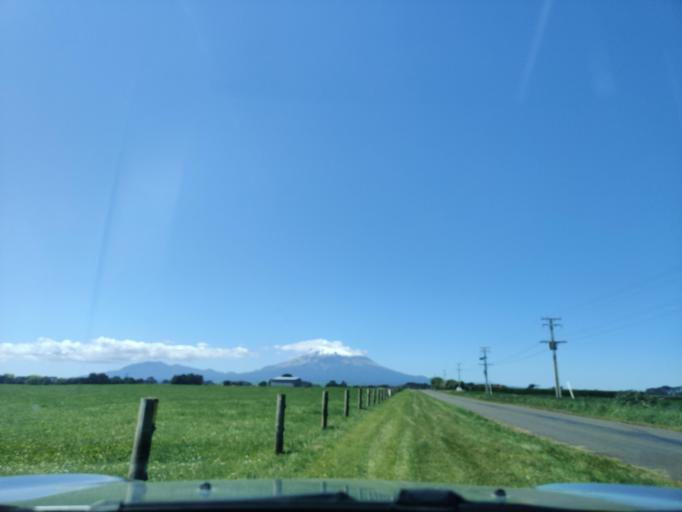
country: NZ
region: Taranaki
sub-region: South Taranaki District
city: Opunake
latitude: -39.3849
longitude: 173.8121
